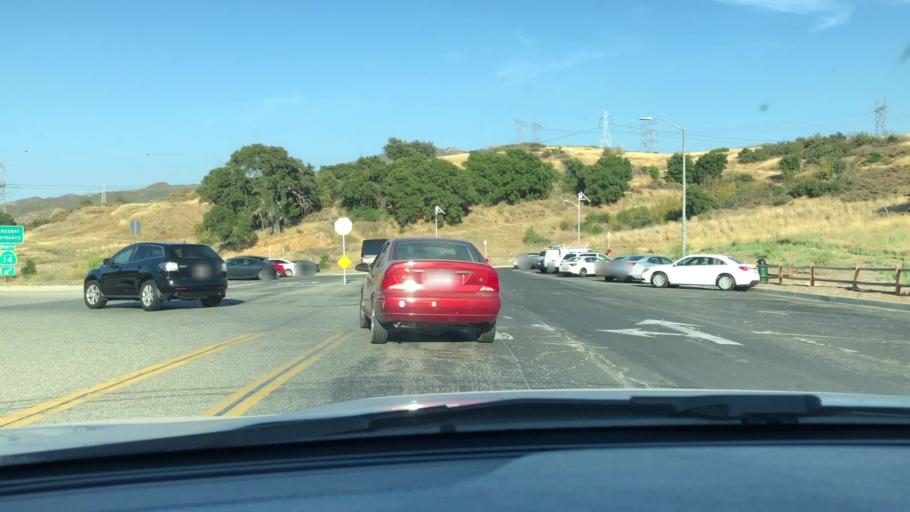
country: US
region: California
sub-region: Los Angeles County
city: Santa Clarita
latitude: 34.3647
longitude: -118.5018
